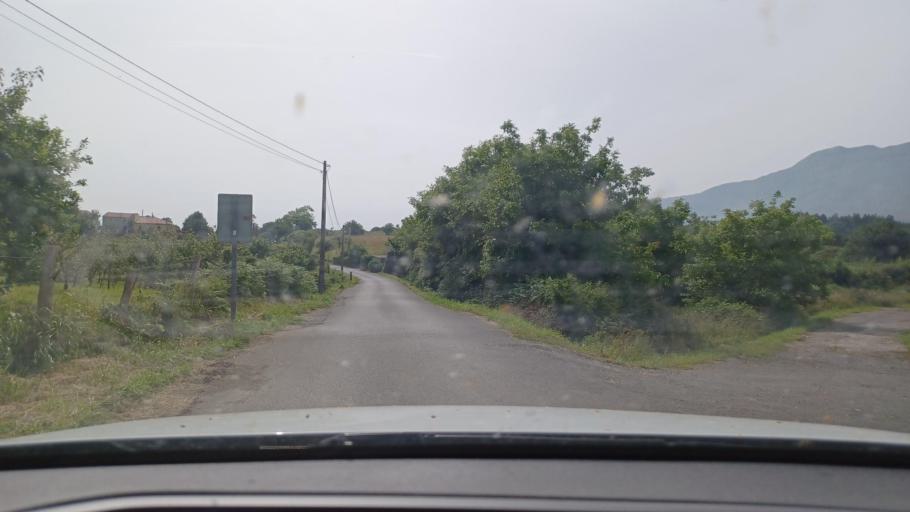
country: ES
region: Asturias
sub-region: Province of Asturias
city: Ribadesella
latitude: 43.4581
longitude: -5.0405
